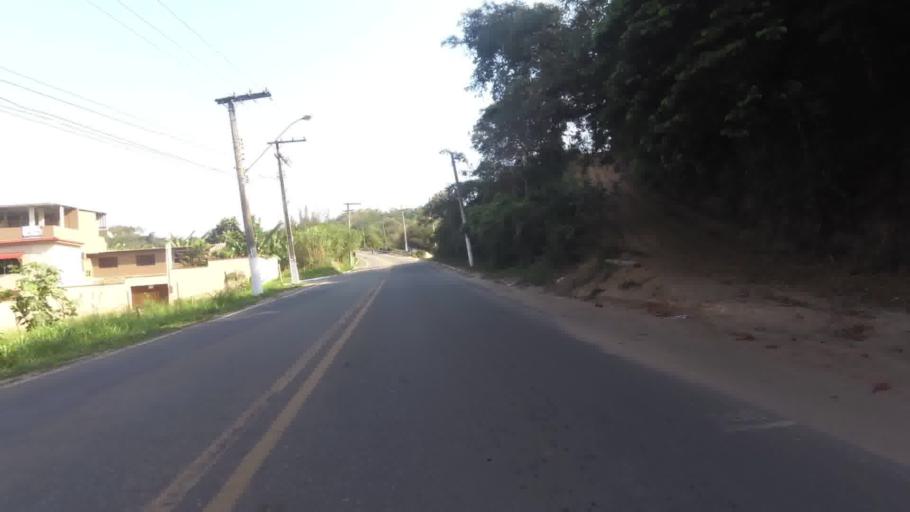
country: BR
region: Espirito Santo
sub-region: Piuma
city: Piuma
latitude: -20.8641
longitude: -40.7598
